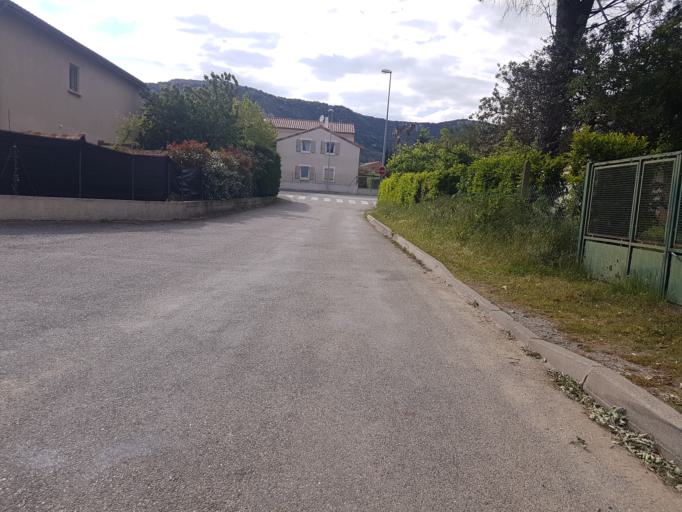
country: FR
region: Rhone-Alpes
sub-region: Departement de l'Ardeche
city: Guilherand-Granges
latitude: 44.9228
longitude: 4.8684
